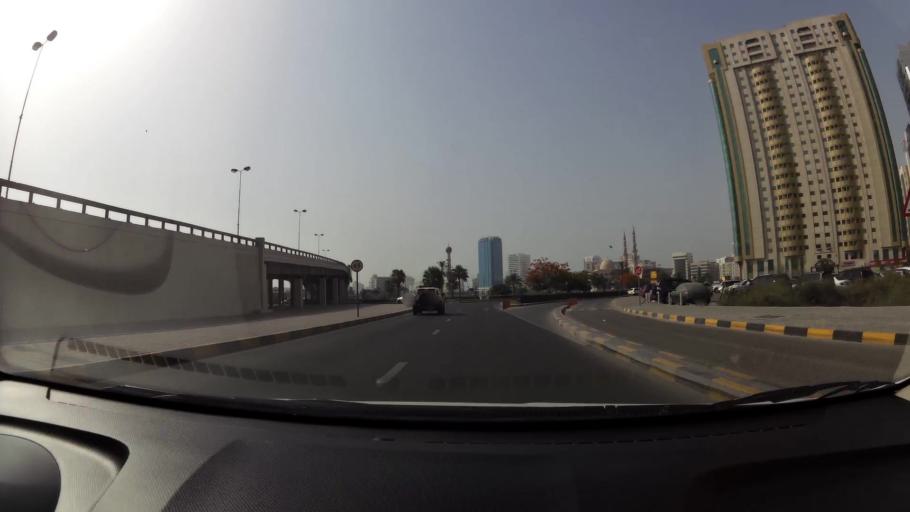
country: AE
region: Ash Shariqah
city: Sharjah
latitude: 25.3453
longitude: 55.3870
